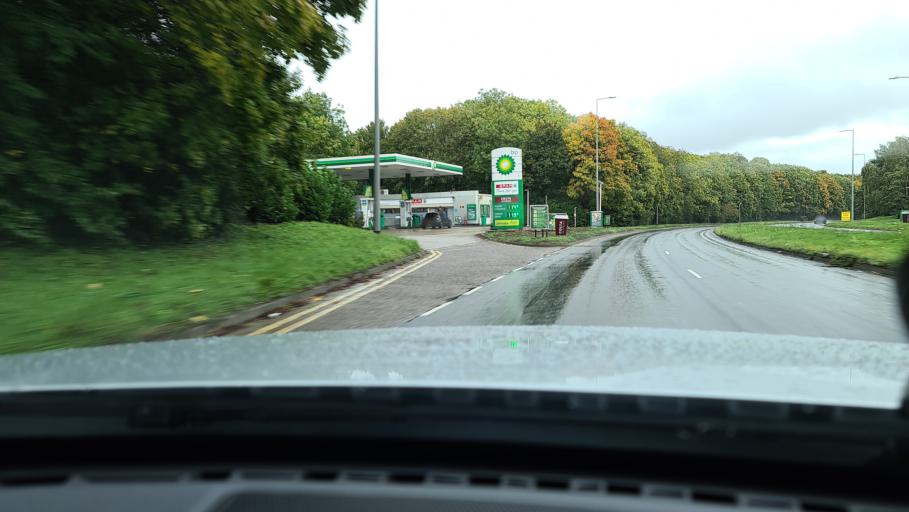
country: GB
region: England
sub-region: Buckinghamshire
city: Bletchley
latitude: 51.9987
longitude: -0.7334
